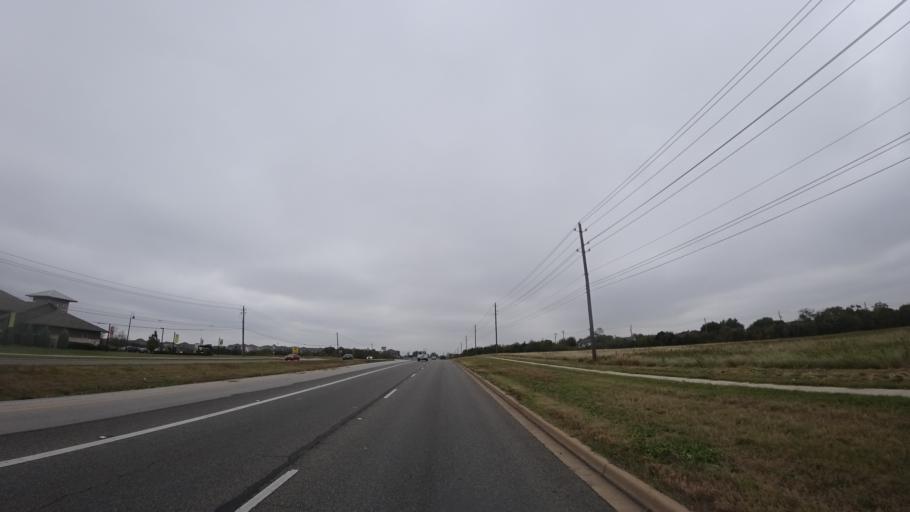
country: US
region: Texas
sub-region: Travis County
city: Pflugerville
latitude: 30.3954
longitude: -97.6540
